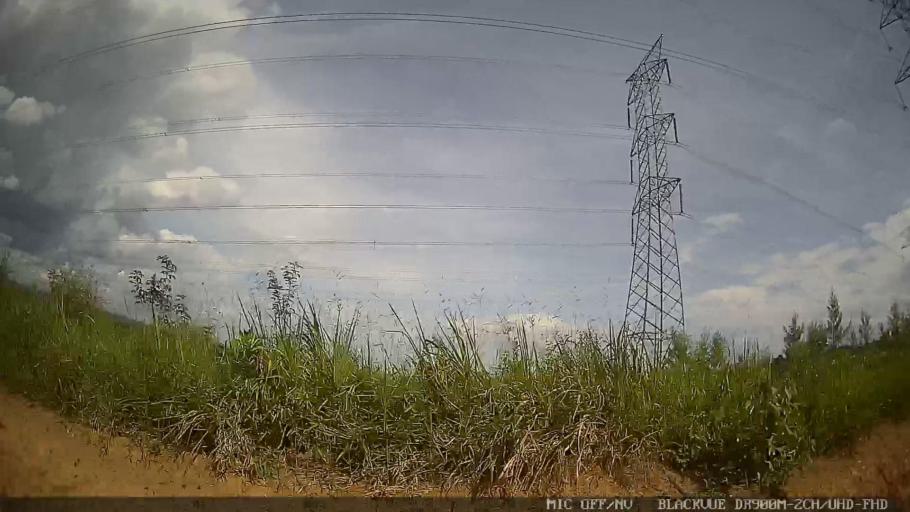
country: BR
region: Sao Paulo
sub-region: Mogi das Cruzes
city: Mogi das Cruzes
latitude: -23.6366
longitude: -46.2118
